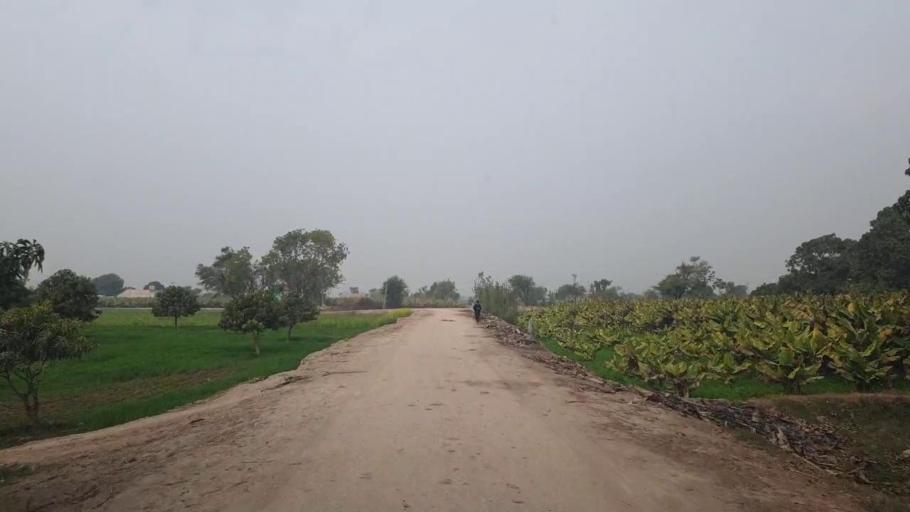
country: PK
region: Sindh
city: Tando Adam
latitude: 25.7136
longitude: 68.6997
